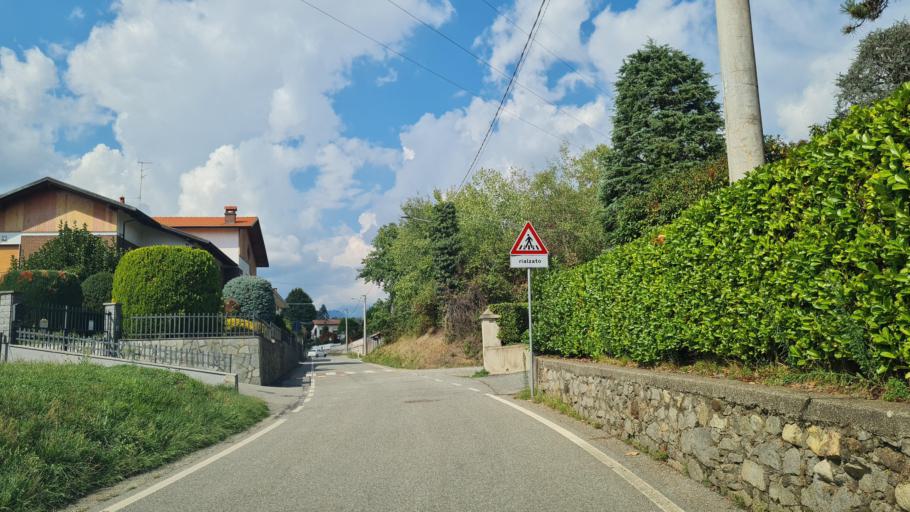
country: IT
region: Piedmont
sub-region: Provincia di Biella
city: Lessona
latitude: 45.5864
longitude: 8.1825
